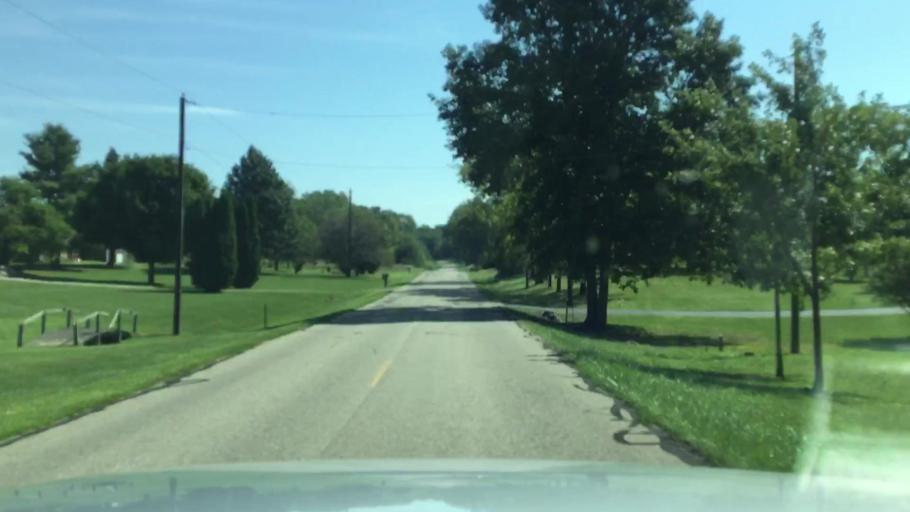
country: US
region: Michigan
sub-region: Lenawee County
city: Manitou Beach-Devils Lake
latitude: 42.0082
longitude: -84.3115
